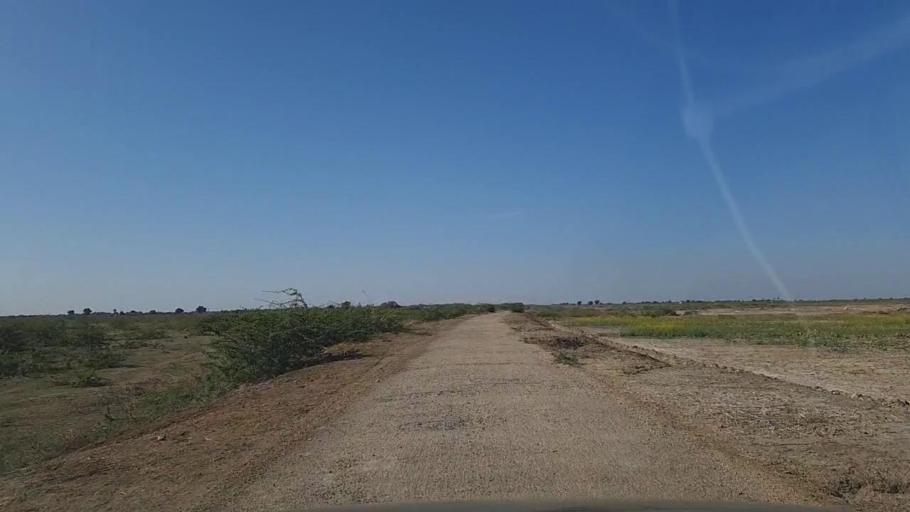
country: PK
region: Sindh
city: Kunri
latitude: 25.2353
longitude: 69.5019
